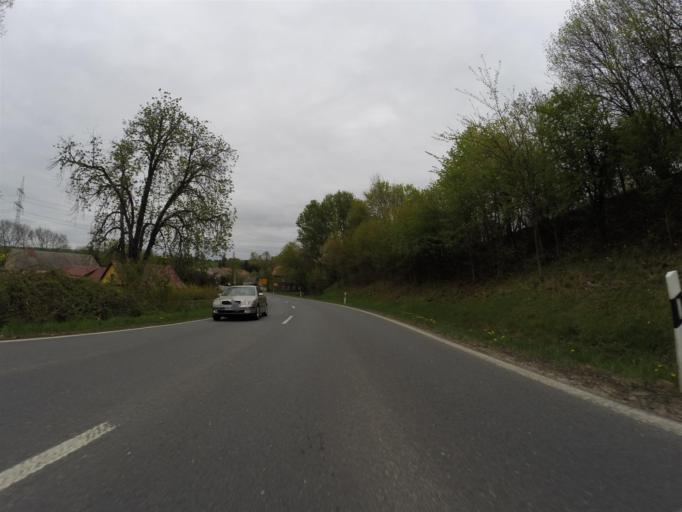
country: DE
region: Thuringia
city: Camburg
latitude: 51.0616
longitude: 11.7220
